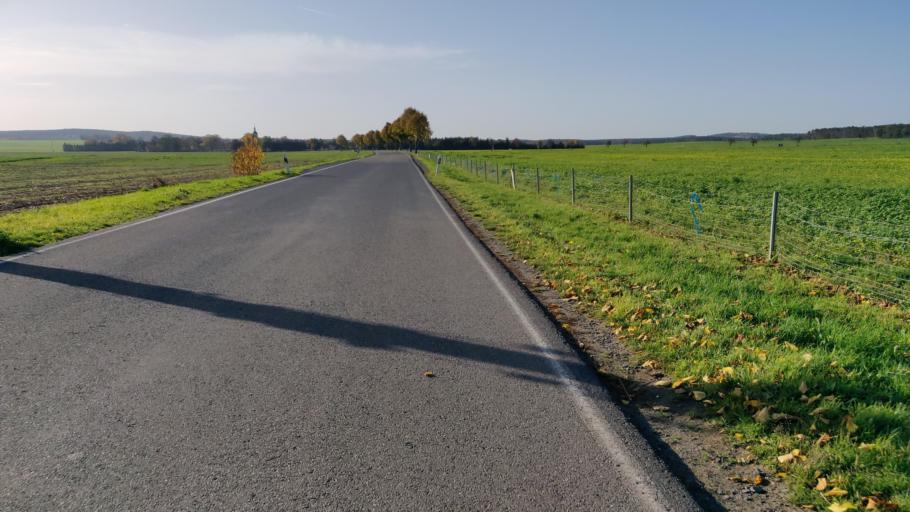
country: DE
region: Brandenburg
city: Kroppen
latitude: 51.3451
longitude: 13.7878
